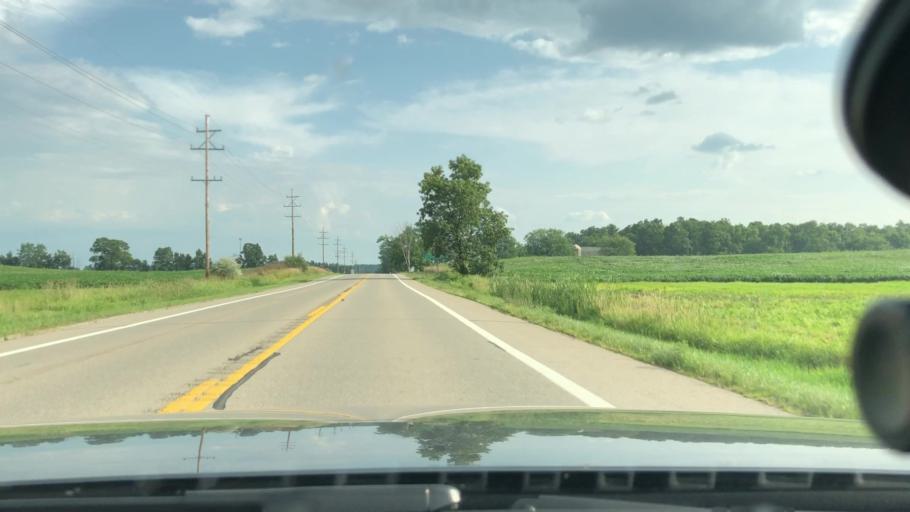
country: US
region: Michigan
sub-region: Washtenaw County
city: Chelsea
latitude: 42.2616
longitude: -84.0341
